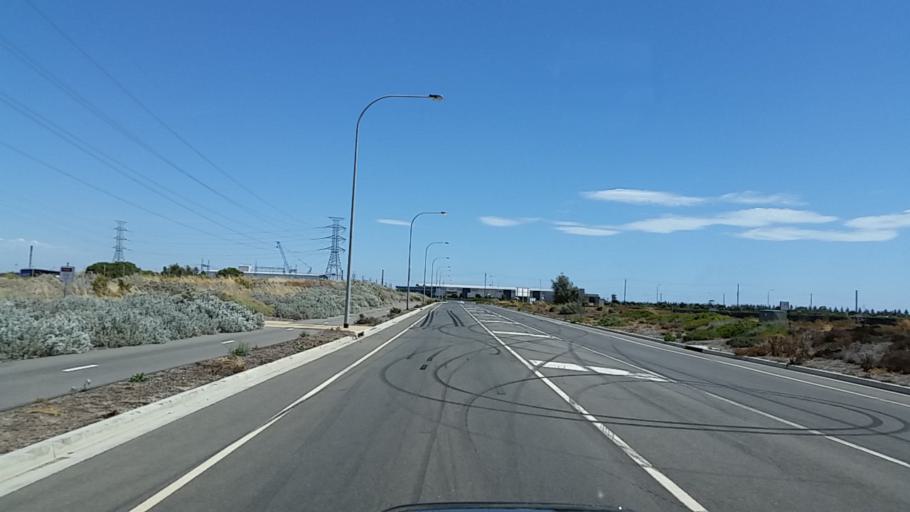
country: AU
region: South Australia
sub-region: Port Adelaide Enfield
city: Birkenhead
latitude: -34.7741
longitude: 138.5092
